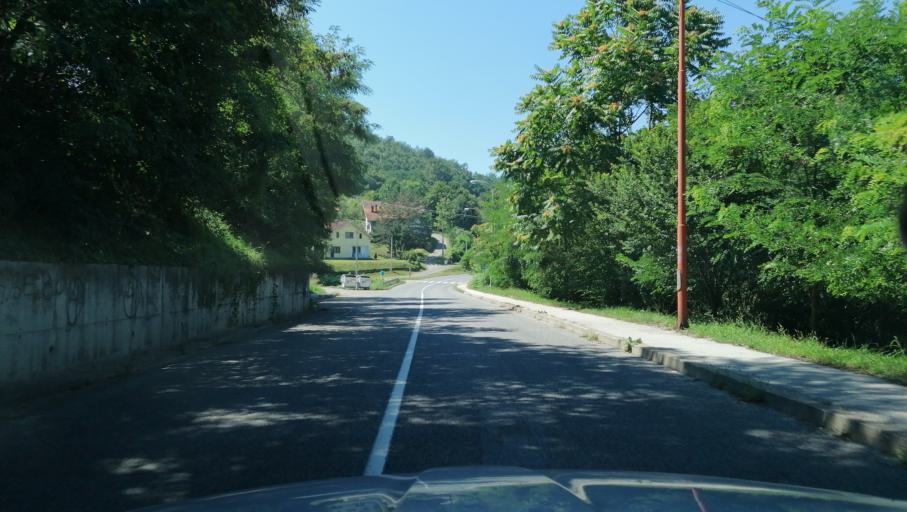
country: RS
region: Central Serbia
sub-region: Raski Okrug
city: Kraljevo
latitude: 43.6894
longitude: 20.6275
